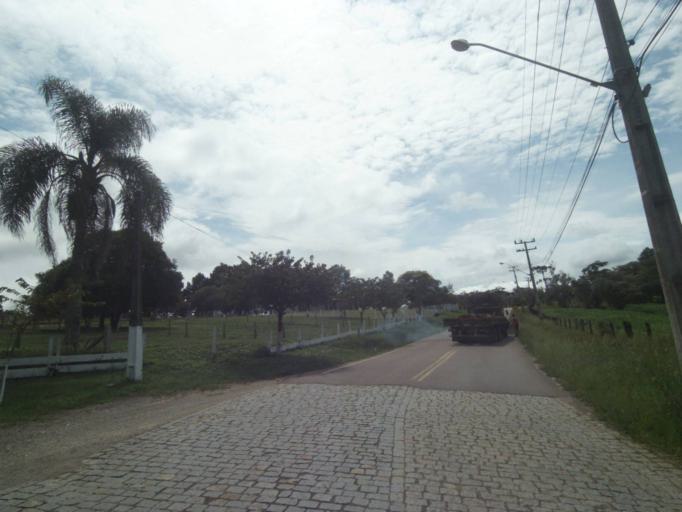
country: BR
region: Parana
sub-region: Campina Grande Do Sul
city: Campina Grande do Sul
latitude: -25.3068
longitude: -49.0448
